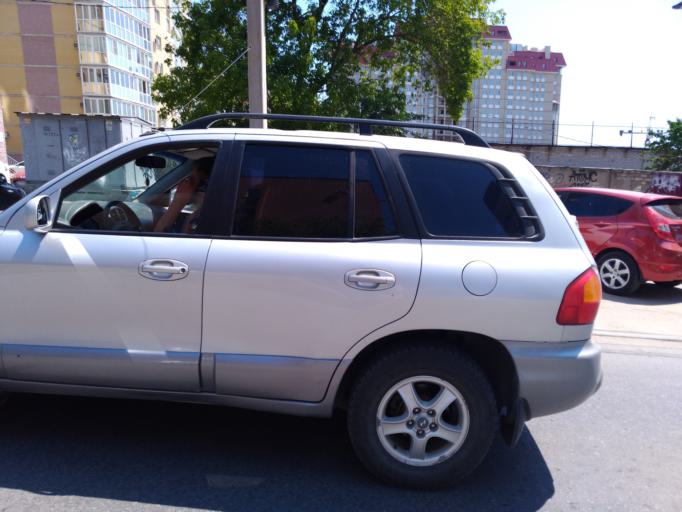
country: RU
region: Volgograd
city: Volgograd
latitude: 48.7148
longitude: 44.5083
